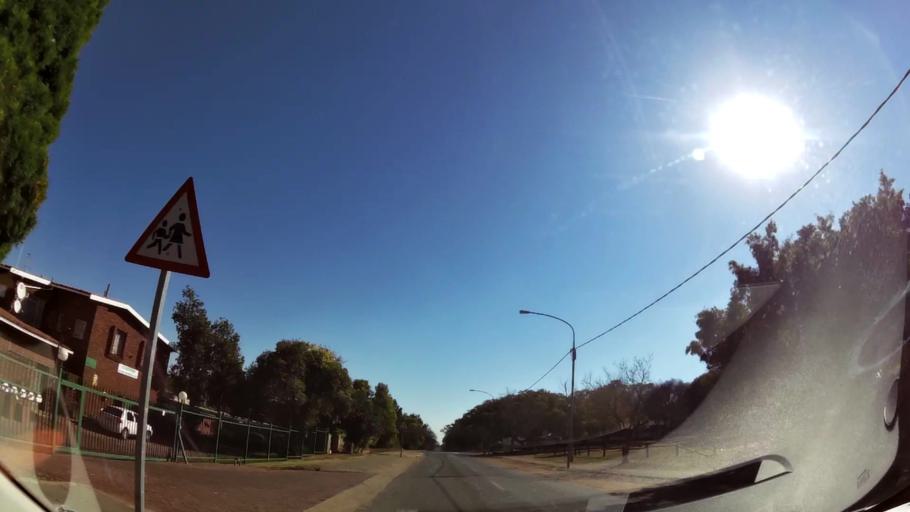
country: ZA
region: Gauteng
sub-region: City of Tshwane Metropolitan Municipality
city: Centurion
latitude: -25.8197
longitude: 28.2077
